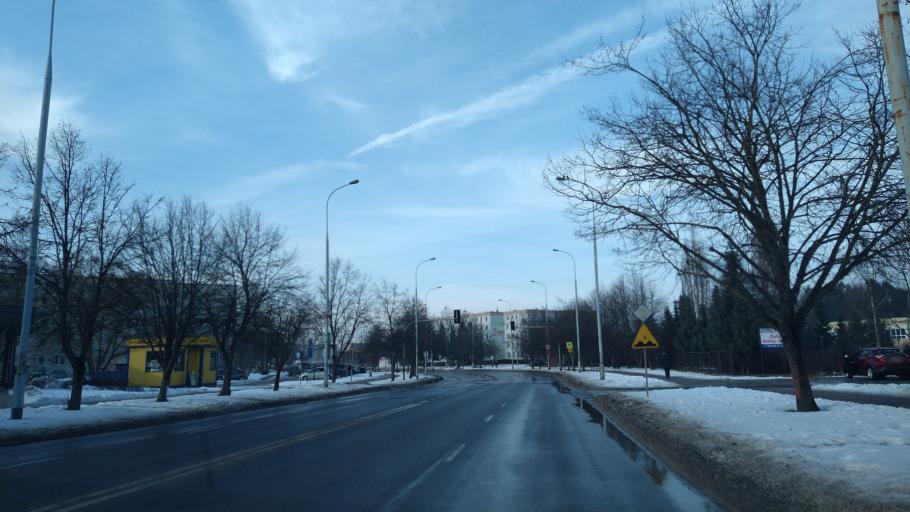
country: PL
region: Warmian-Masurian Voivodeship
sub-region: Powiat olsztynski
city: Olsztyn
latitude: 53.7416
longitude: 20.5140
